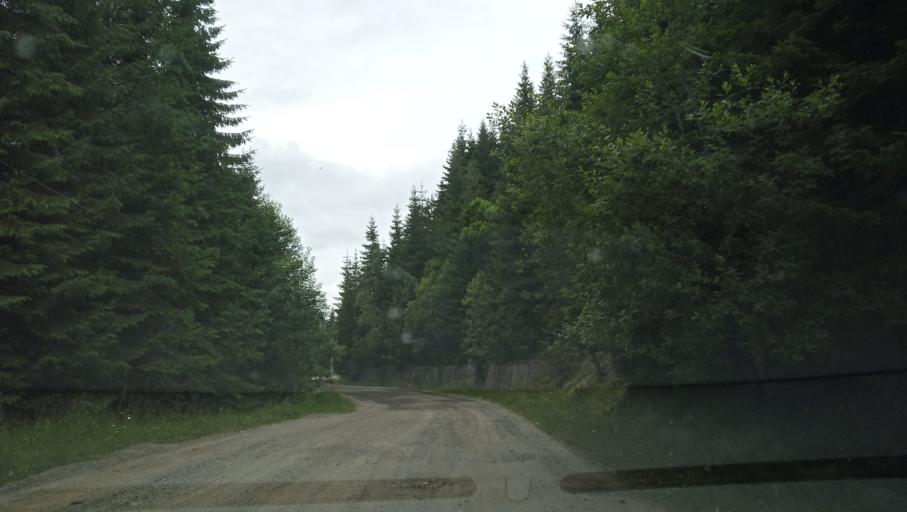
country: RO
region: Valcea
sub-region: Comuna Voineasa
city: Voineasa
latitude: 45.4253
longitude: 23.7607
